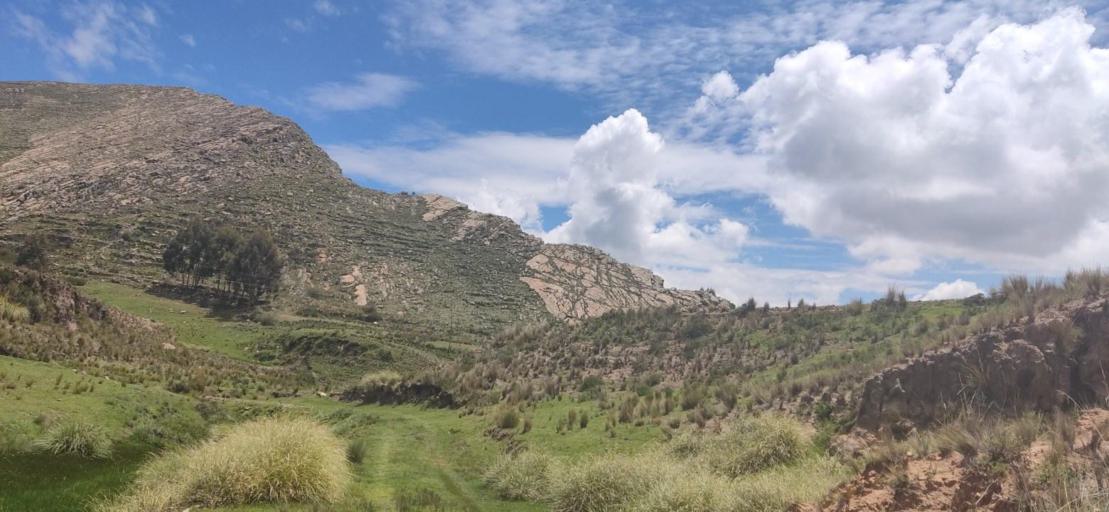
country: BO
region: La Paz
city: Batallas
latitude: -16.3468
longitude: -68.6444
